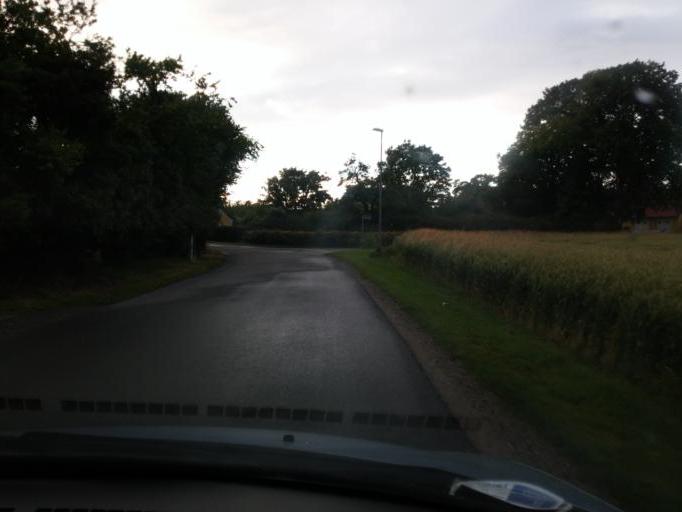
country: DK
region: South Denmark
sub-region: Kerteminde Kommune
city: Munkebo
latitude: 55.5139
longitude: 10.6137
